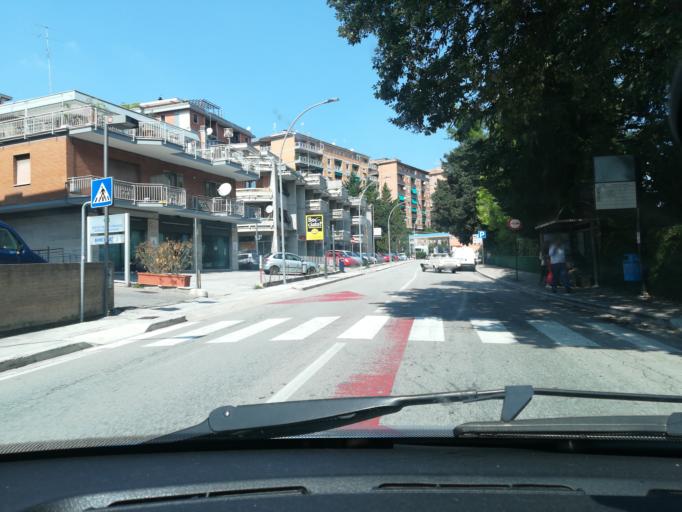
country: IT
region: The Marches
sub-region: Provincia di Macerata
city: Macerata
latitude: 43.2928
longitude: 13.4373
